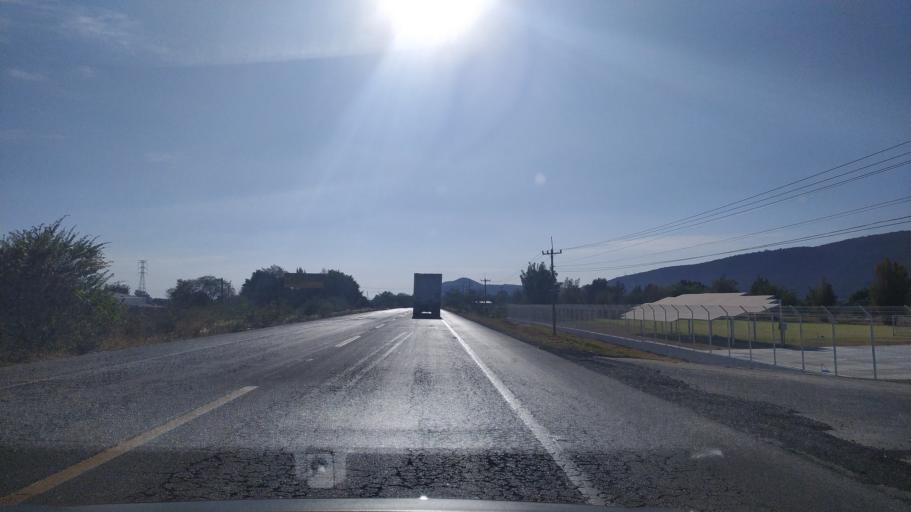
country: MX
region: Jalisco
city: Jamay
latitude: 20.2940
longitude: -102.6596
